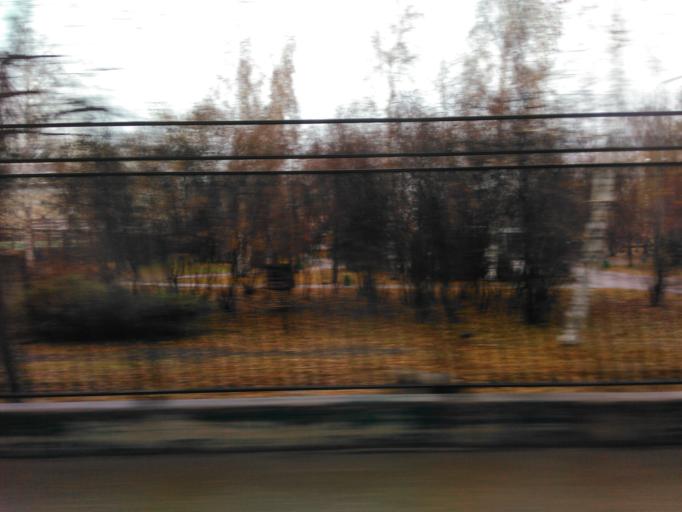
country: RU
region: Tatarstan
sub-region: Gorod Kazan'
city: Kazan
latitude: 55.7991
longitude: 49.0604
